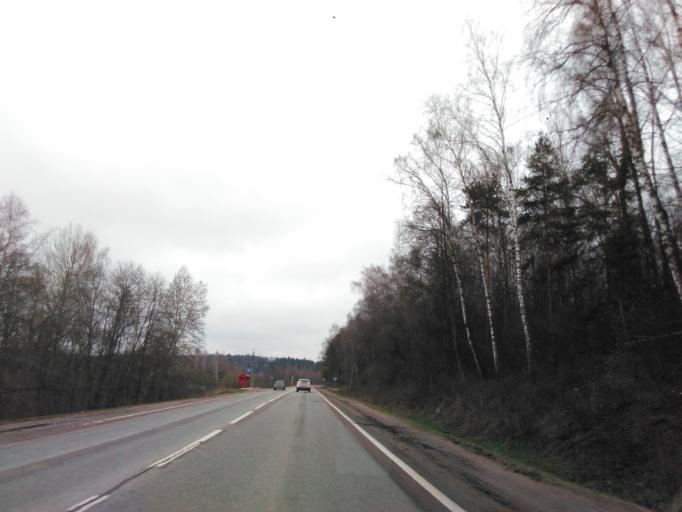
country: RU
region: Moskovskaya
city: Snegiri
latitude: 55.8487
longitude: 36.9541
